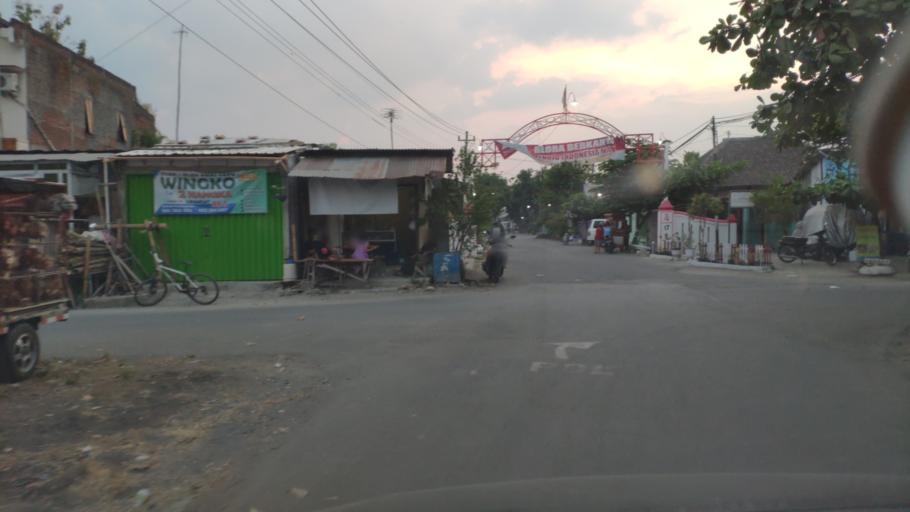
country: ID
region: Central Java
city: Cepu
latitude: -7.1535
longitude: 111.5900
